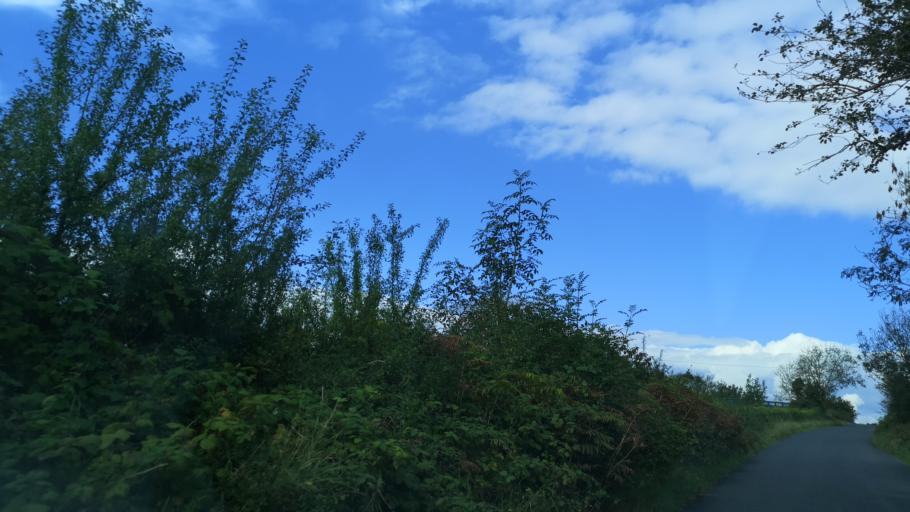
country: IE
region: Connaught
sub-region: County Galway
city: Athenry
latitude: 53.2359
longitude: -8.7436
